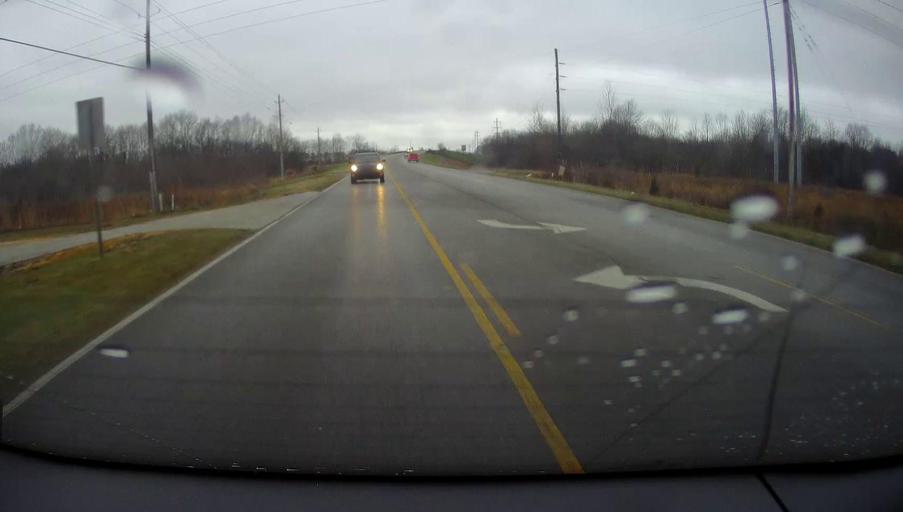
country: US
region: Mississippi
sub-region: Alcorn County
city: Corinth
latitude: 34.9092
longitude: -88.5095
